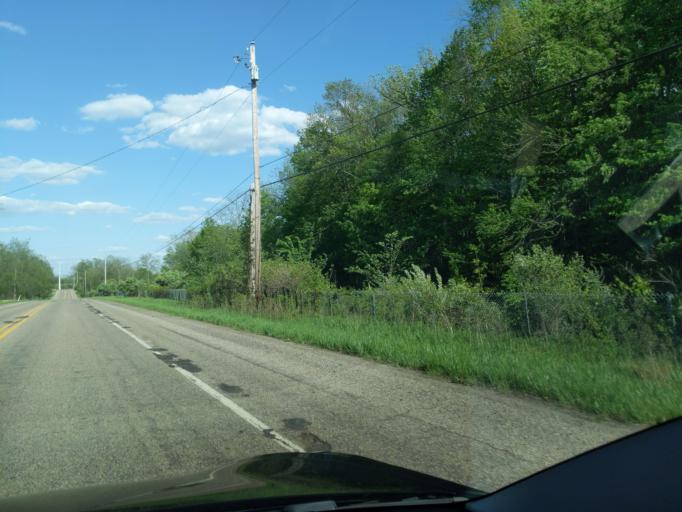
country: US
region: Michigan
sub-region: Eaton County
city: Dimondale
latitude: 42.6829
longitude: -84.6716
